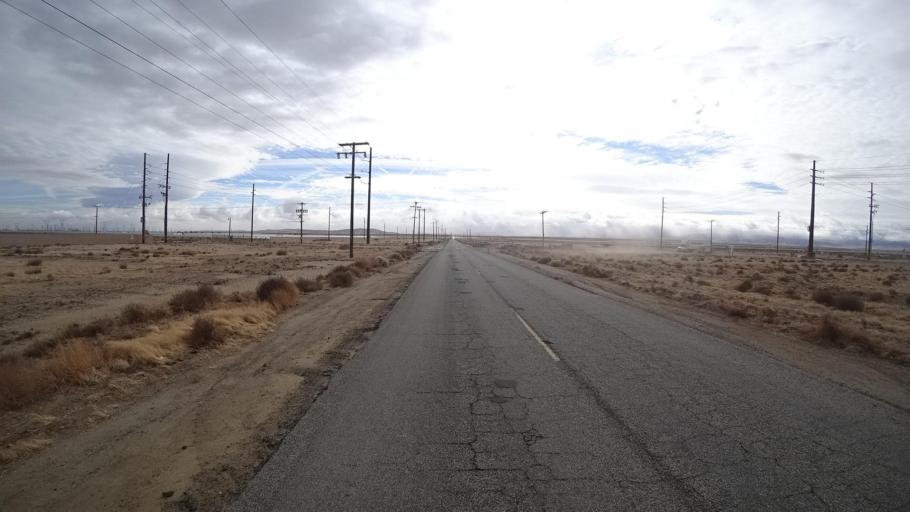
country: US
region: California
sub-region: Los Angeles County
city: Green Valley
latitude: 34.8341
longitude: -118.4318
